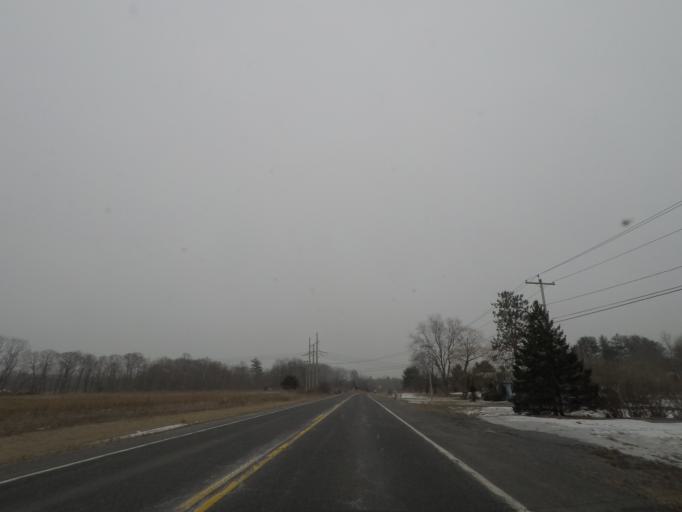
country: US
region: New York
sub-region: Albany County
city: Delmar
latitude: 42.5604
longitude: -73.8158
